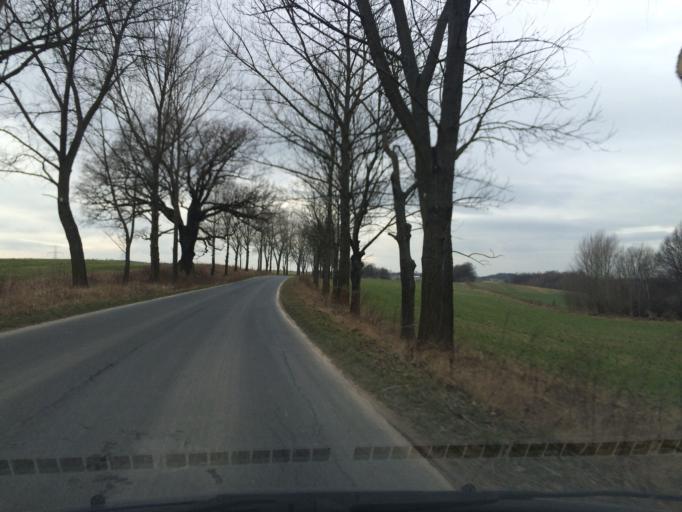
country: PL
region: Lower Silesian Voivodeship
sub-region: Powiat lwowecki
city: Lwowek Slaski
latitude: 51.1212
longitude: 15.5043
